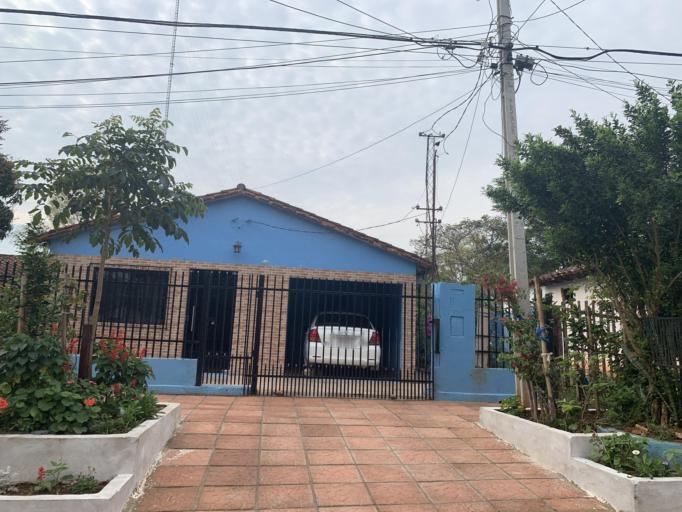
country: PY
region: Misiones
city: San Juan Bautista
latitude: -26.6644
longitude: -57.1488
